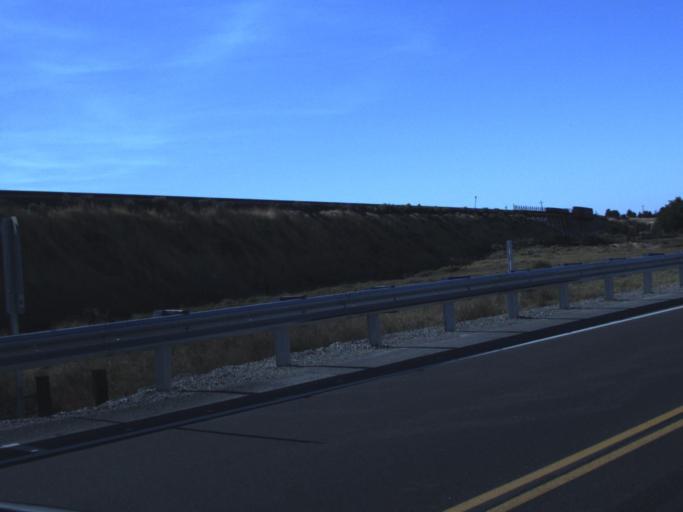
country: US
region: Washington
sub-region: Franklin County
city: Pasco
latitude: 46.1956
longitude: -119.0847
